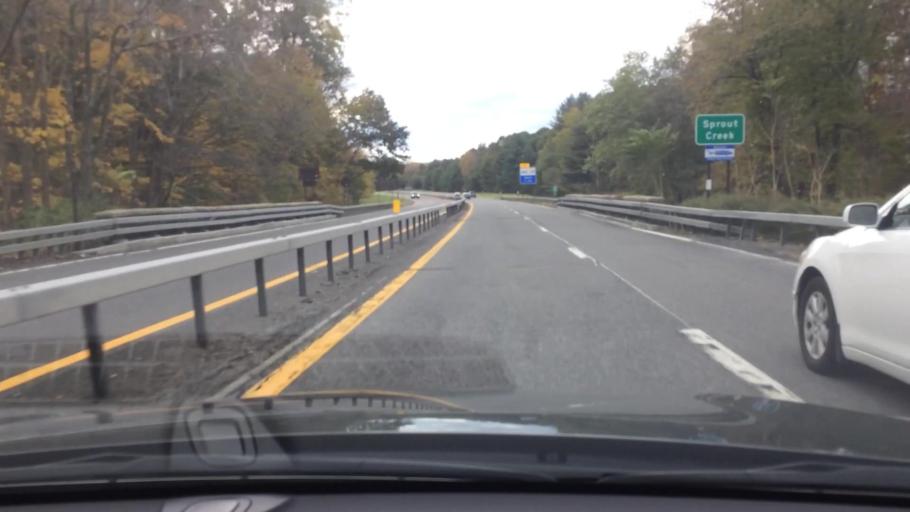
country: US
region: New York
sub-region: Dutchess County
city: Hillside Lake
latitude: 41.6664
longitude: -73.7897
